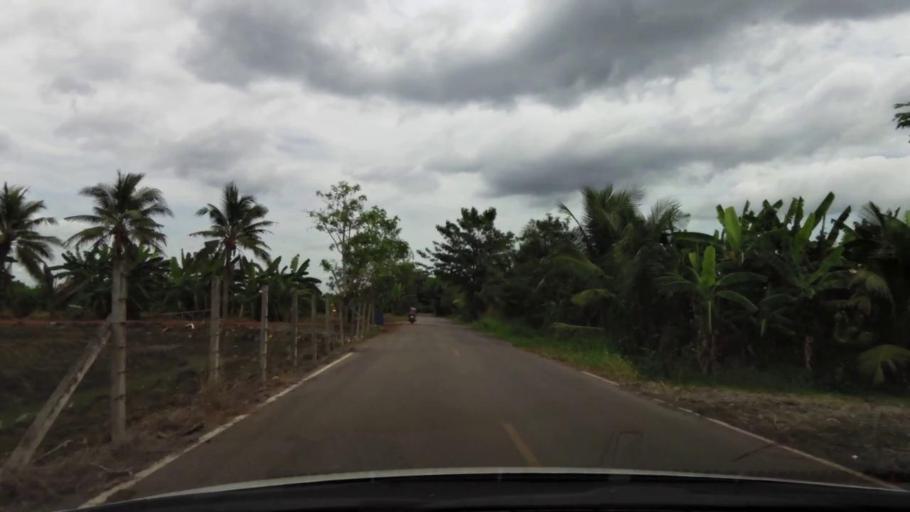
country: TH
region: Samut Sakhon
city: Ban Phaeo
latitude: 13.5648
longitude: 100.0335
